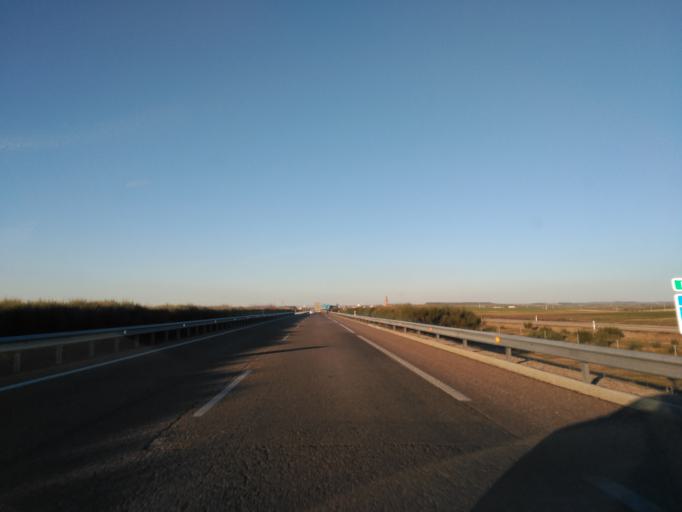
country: ES
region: Castille and Leon
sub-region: Provincia de Valladolid
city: Alaejos
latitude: 41.2877
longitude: -5.2409
